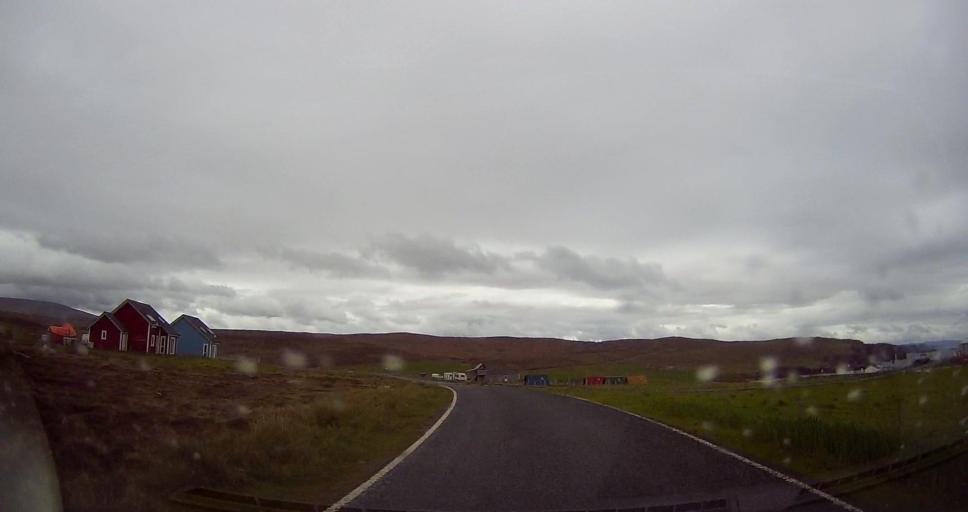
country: GB
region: Scotland
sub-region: Shetland Islands
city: Lerwick
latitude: 60.4941
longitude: -1.5621
